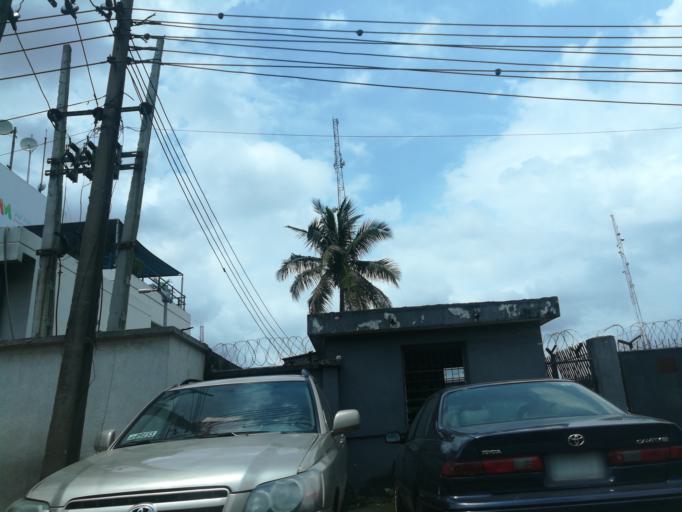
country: NG
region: Lagos
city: Oshodi
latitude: 6.5546
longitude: 3.3562
